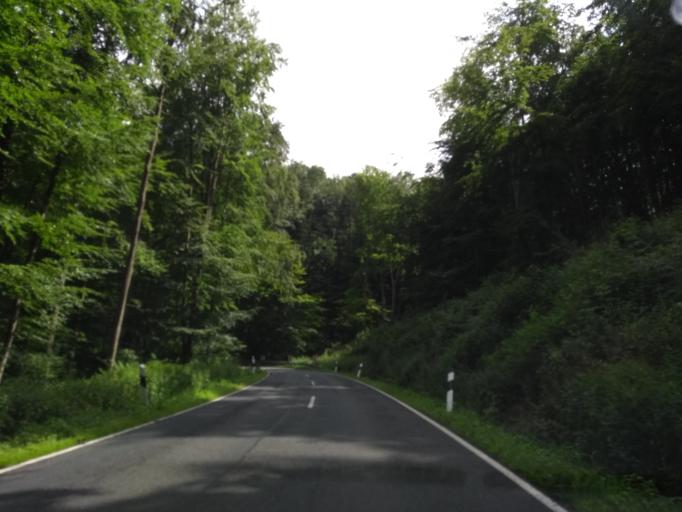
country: DE
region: Lower Saxony
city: Bad Pyrmont
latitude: 51.9662
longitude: 9.2975
